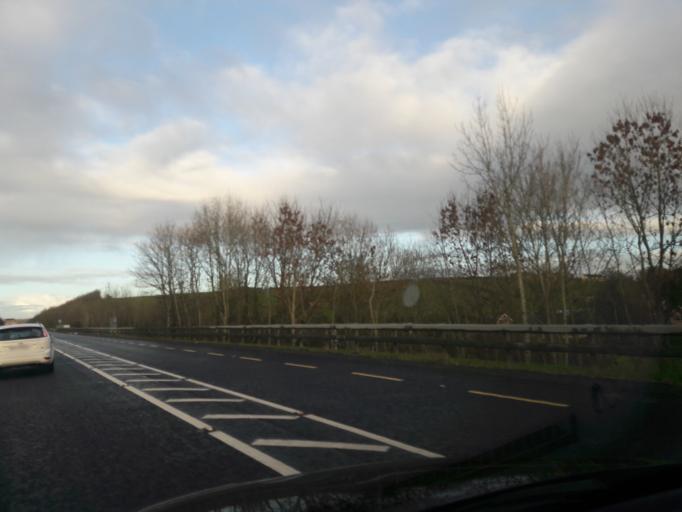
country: IE
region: Ulster
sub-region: County Monaghan
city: Carrickmacross
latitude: 53.9960
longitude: -6.7171
